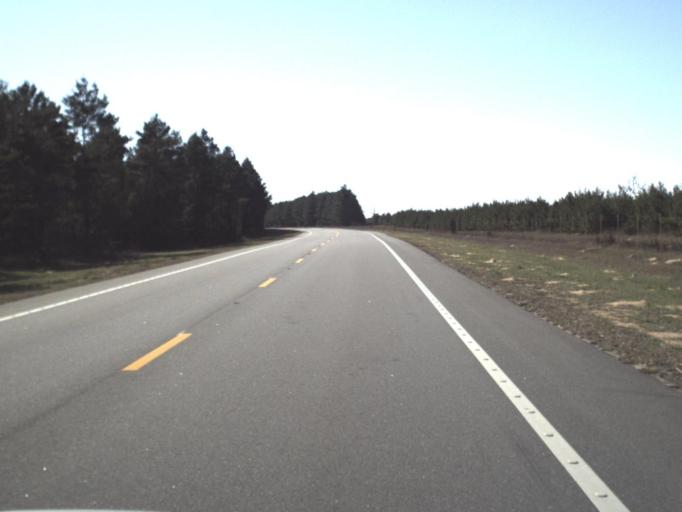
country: US
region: Florida
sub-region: Bay County
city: Youngstown
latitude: 30.4341
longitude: -85.2739
